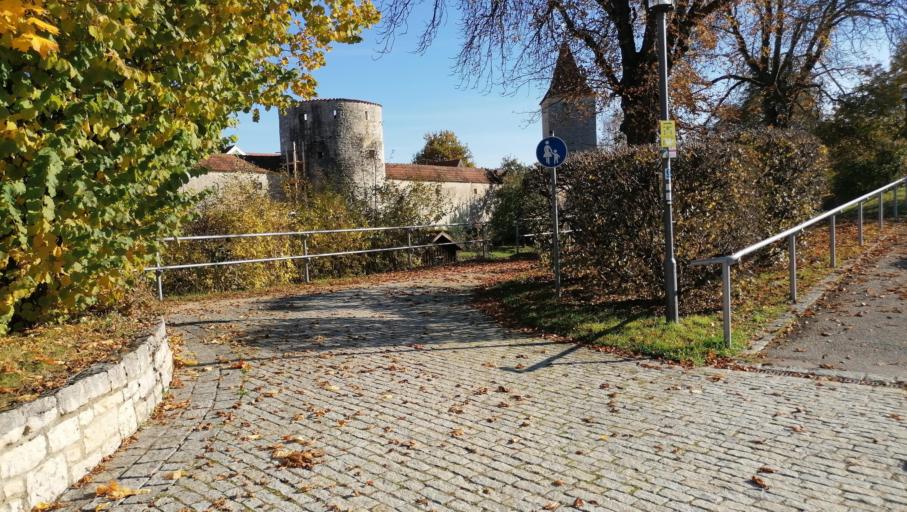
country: DE
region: Bavaria
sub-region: Upper Palatinate
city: Berching
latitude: 49.1066
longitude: 11.4376
